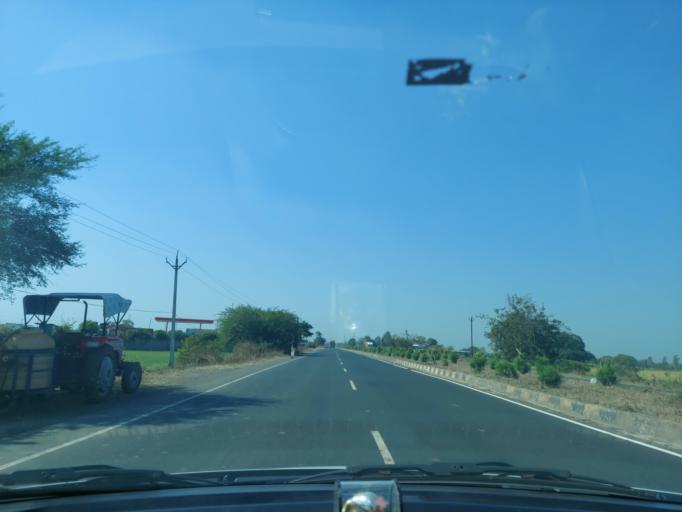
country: IN
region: Madhya Pradesh
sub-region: Indore
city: Manpur
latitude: 22.4445
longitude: 75.6033
